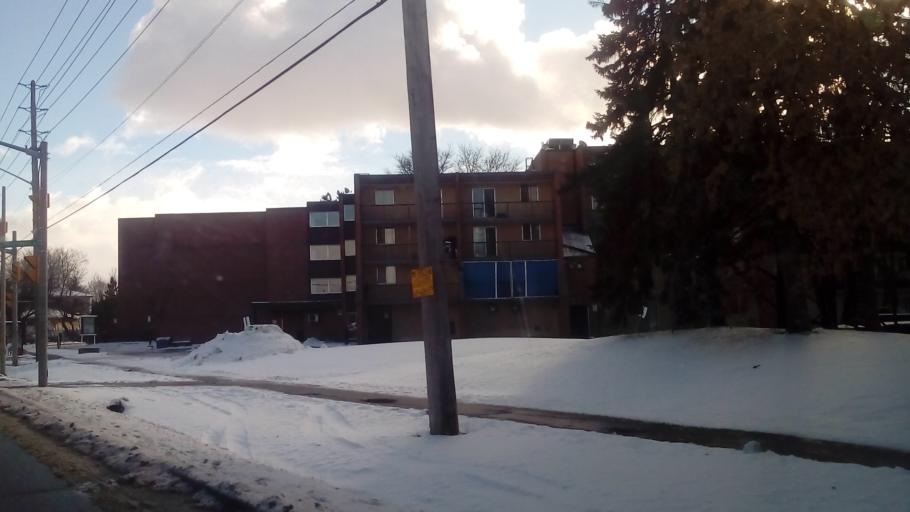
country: CA
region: Ontario
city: Ottawa
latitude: 45.3986
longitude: -75.6191
